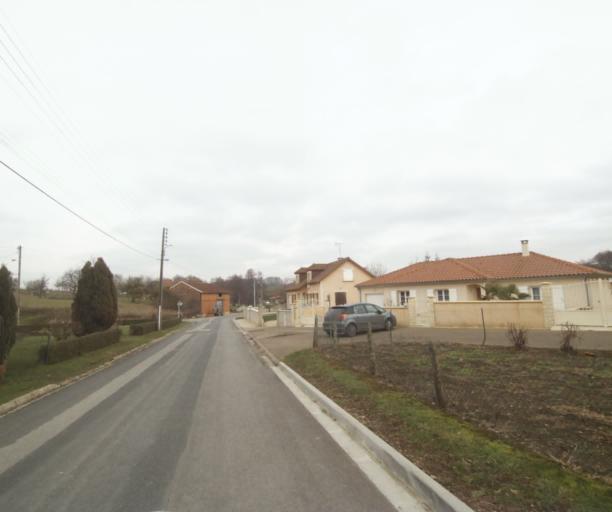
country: FR
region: Champagne-Ardenne
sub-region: Departement de la Marne
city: Sermaize-les-Bains
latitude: 48.7378
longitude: 4.9045
